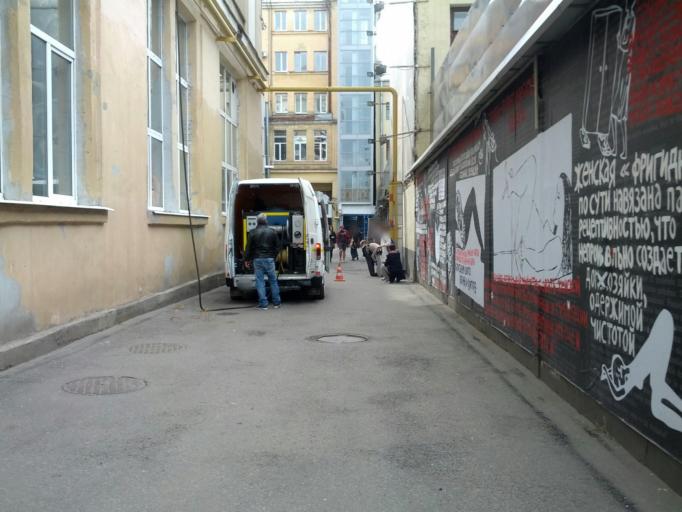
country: RU
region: St.-Petersburg
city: Centralniy
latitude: 59.9219
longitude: 30.3567
